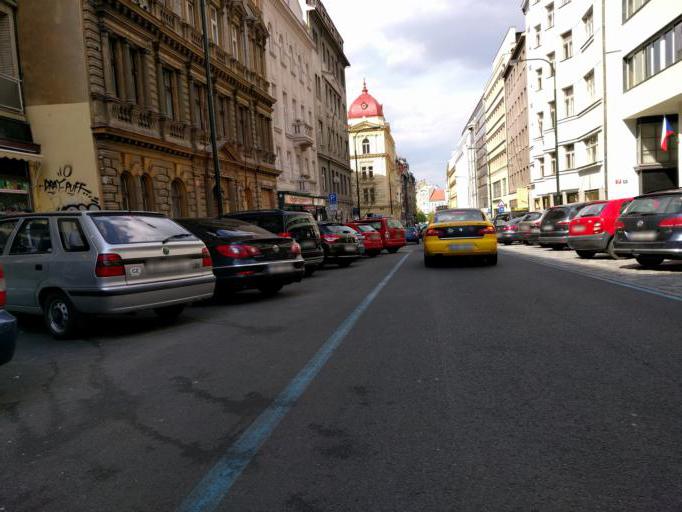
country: CZ
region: Praha
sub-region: Praha 1
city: Stare Mesto
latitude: 50.0789
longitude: 14.4254
